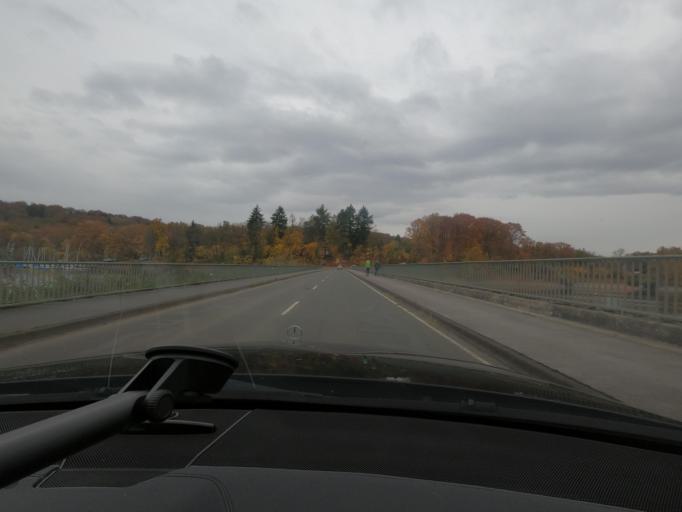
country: DE
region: North Rhine-Westphalia
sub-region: Regierungsbezirk Arnsberg
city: Mohnesee
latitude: 51.4884
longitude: 8.1540
